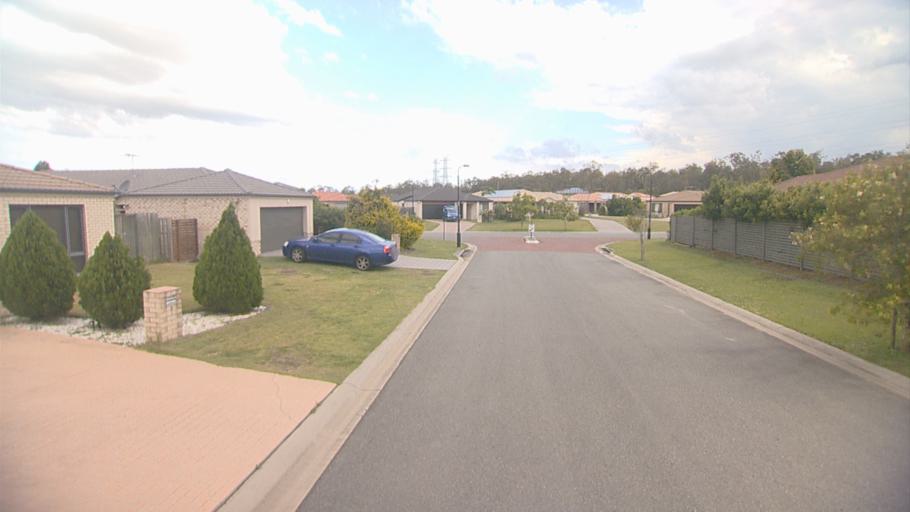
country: AU
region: Queensland
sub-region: Logan
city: Woodridge
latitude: -27.6574
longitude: 153.0749
